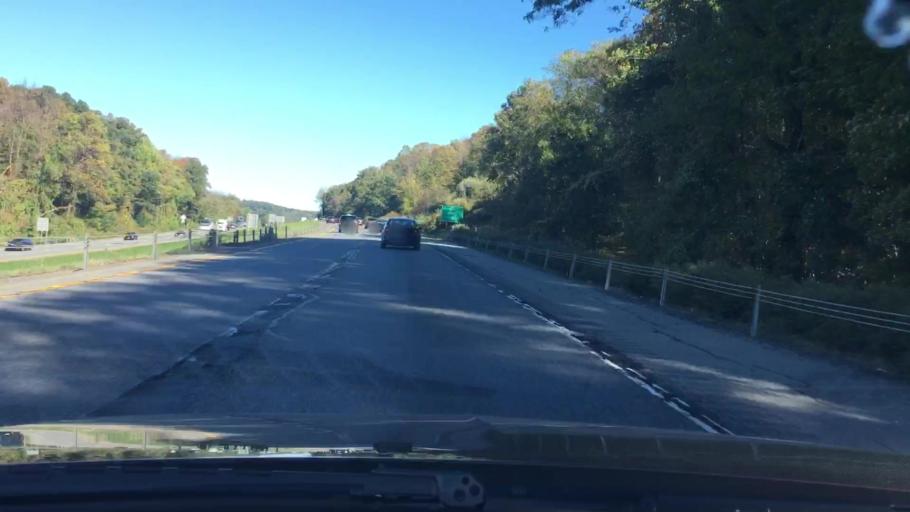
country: US
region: New York
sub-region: Putnam County
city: Peach Lake
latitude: 41.3855
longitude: -73.5541
